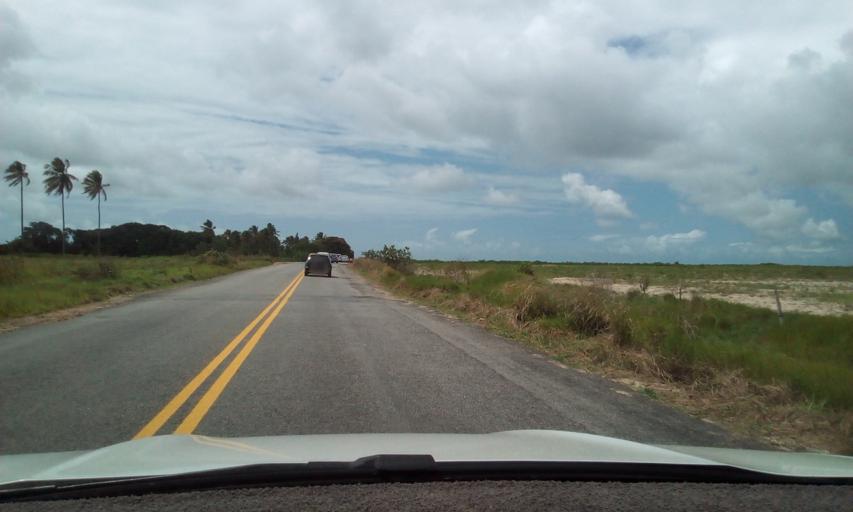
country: BR
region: Paraiba
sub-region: Rio Tinto
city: Rio Tinto
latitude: -6.7716
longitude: -35.0325
